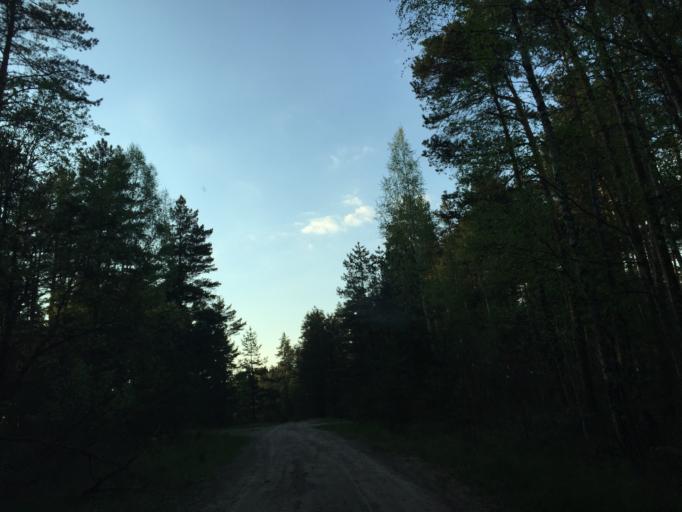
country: LV
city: Tireli
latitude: 56.8680
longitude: 23.6874
